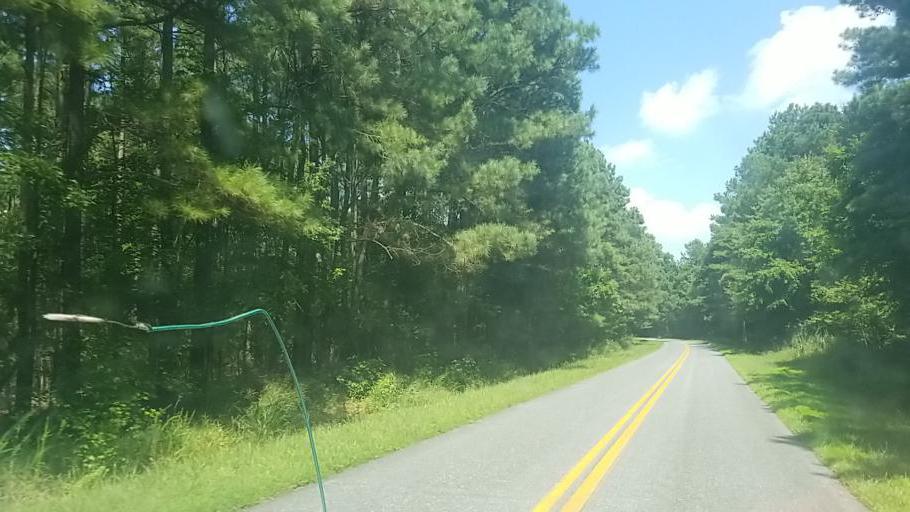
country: US
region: Maryland
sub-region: Wicomico County
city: Hebron
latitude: 38.4272
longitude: -75.8610
